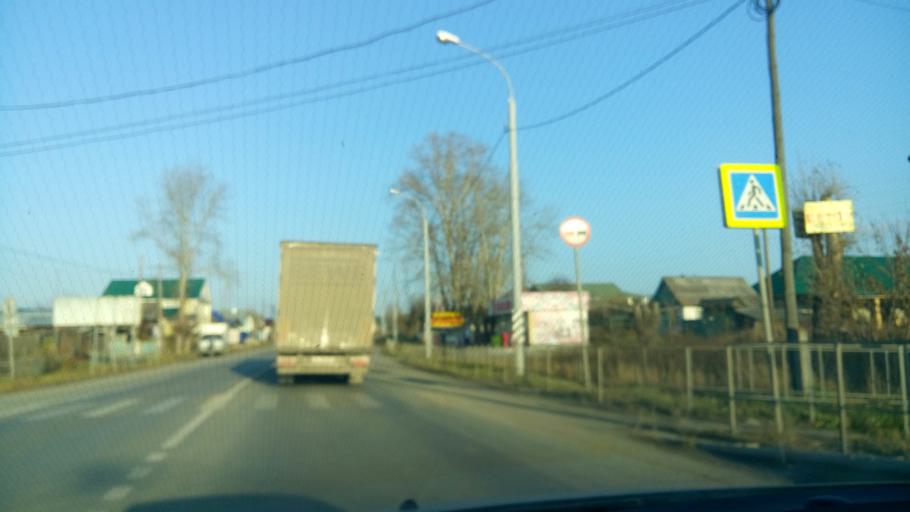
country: RU
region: Sverdlovsk
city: Beloyarskiy
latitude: 56.7648
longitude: 61.4226
